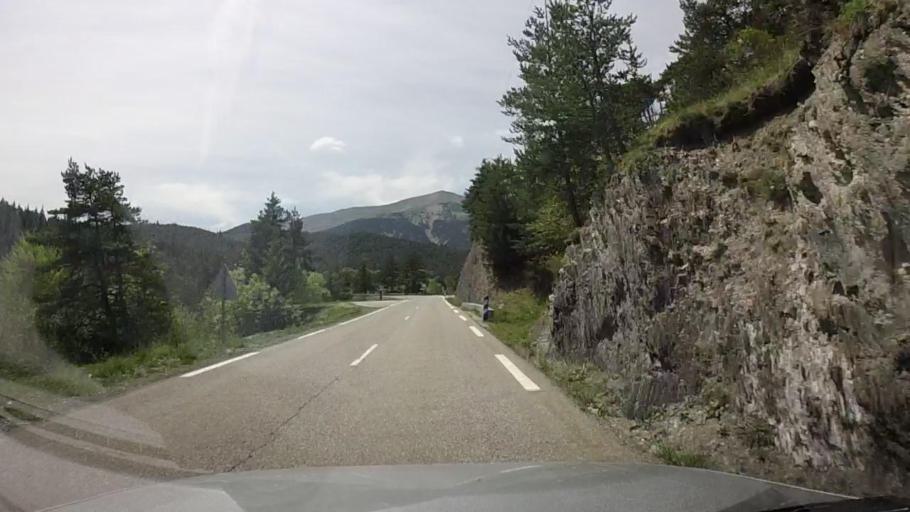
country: FR
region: Provence-Alpes-Cote d'Azur
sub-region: Departement des Alpes-de-Haute-Provence
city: Seyne-les-Alpes
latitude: 44.2641
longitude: 6.3610
